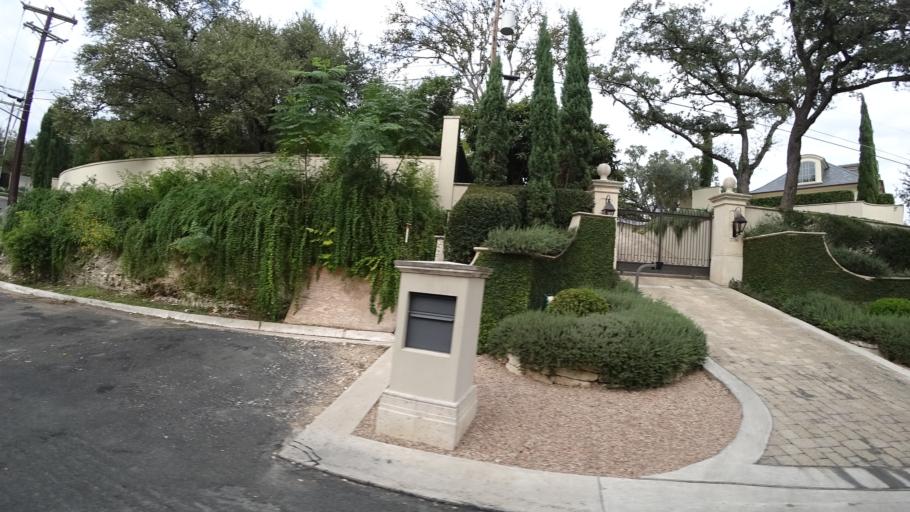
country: US
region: Texas
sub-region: Travis County
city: Rollingwood
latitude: 30.2794
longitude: -97.7819
